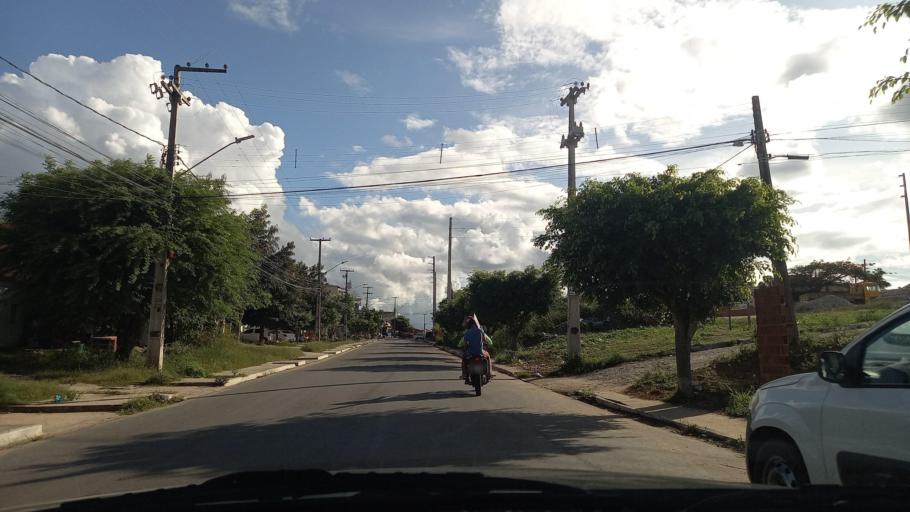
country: BR
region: Pernambuco
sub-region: Gravata
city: Gravata
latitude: -8.2052
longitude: -35.5786
